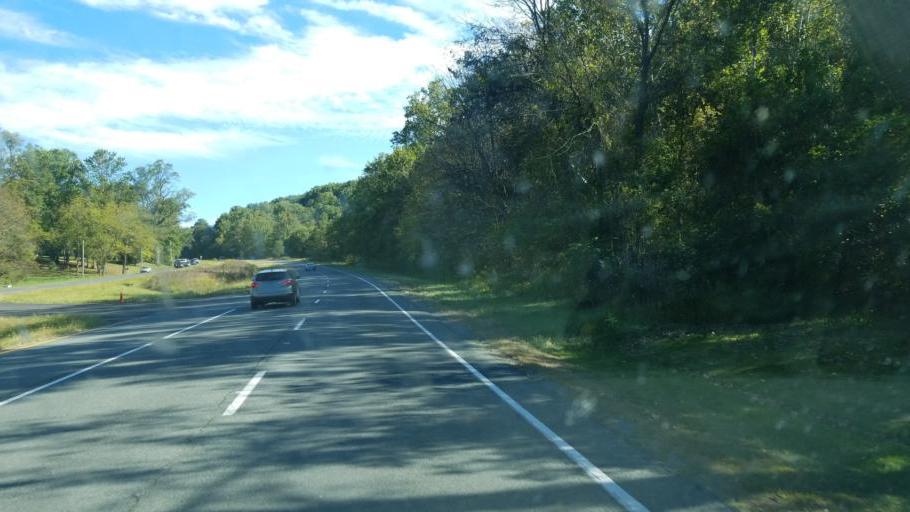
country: US
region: Virginia
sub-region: Warren County
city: Shenandoah Farms
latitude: 39.0224
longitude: -77.9737
